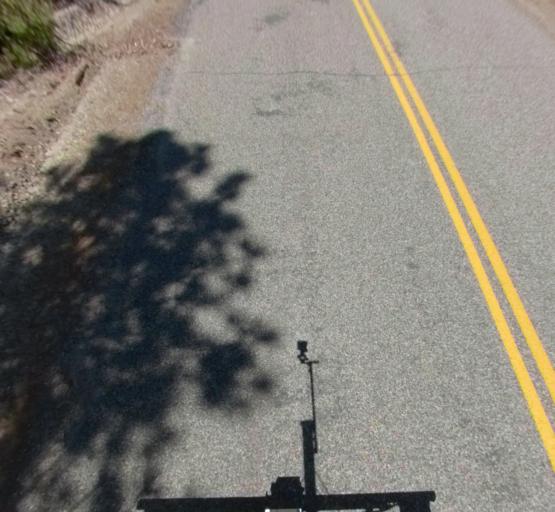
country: US
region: California
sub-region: Madera County
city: Oakhurst
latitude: 37.3433
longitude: -119.5520
